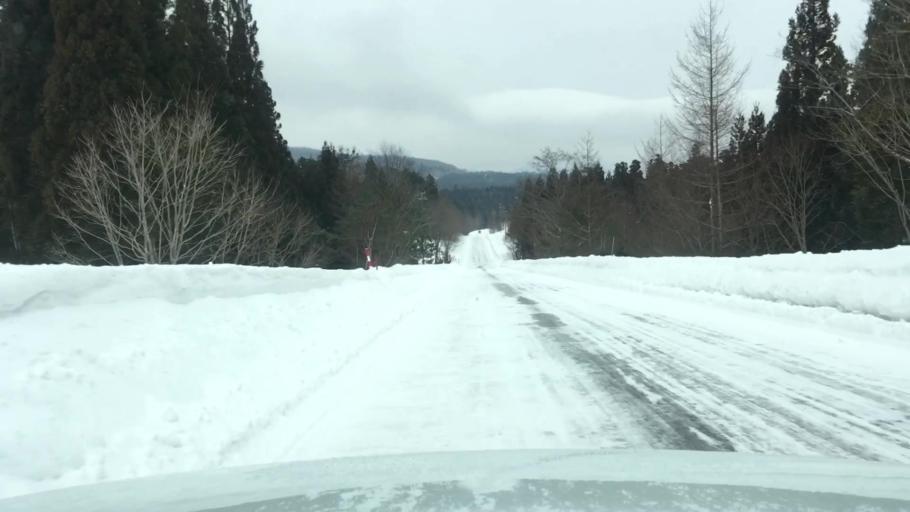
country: JP
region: Akita
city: Hanawa
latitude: 39.9857
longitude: 141.0018
